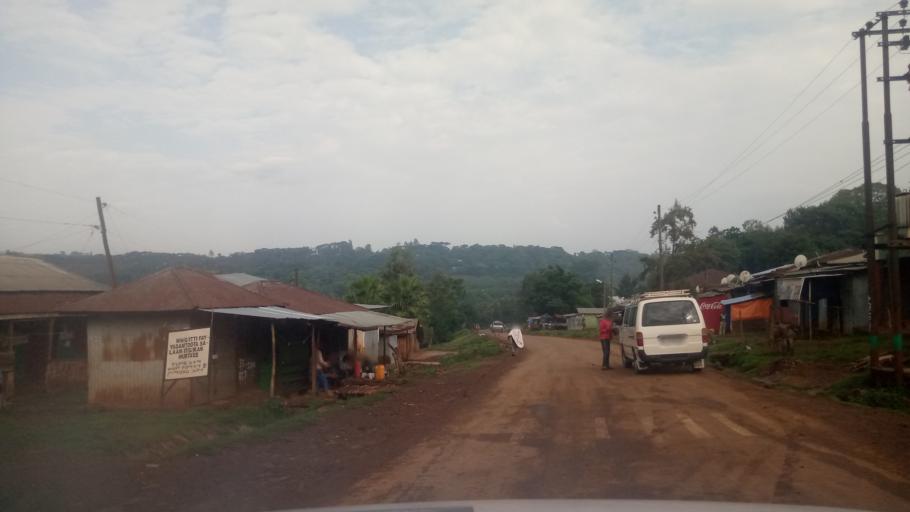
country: ET
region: Oromiya
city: Agaro
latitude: 7.8380
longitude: 36.6693
